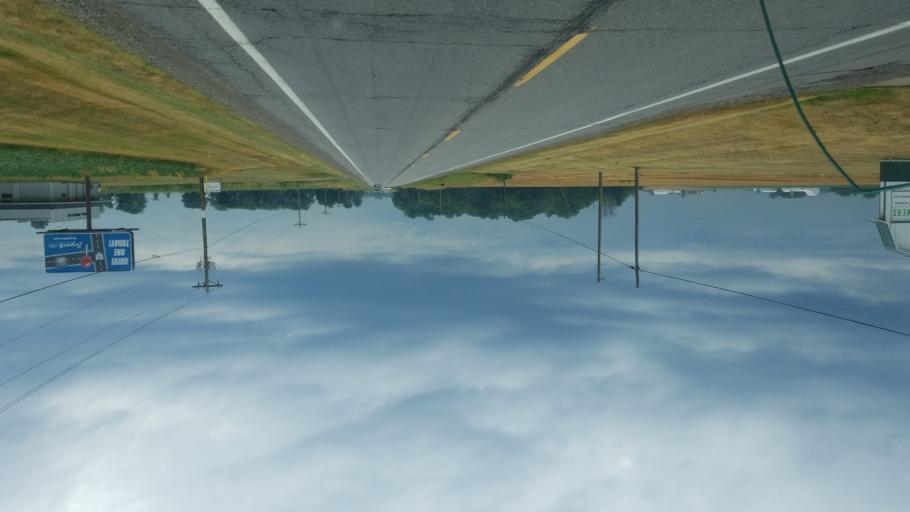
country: US
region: Ohio
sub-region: Williams County
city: Edgerton
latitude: 41.4481
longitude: -84.7063
